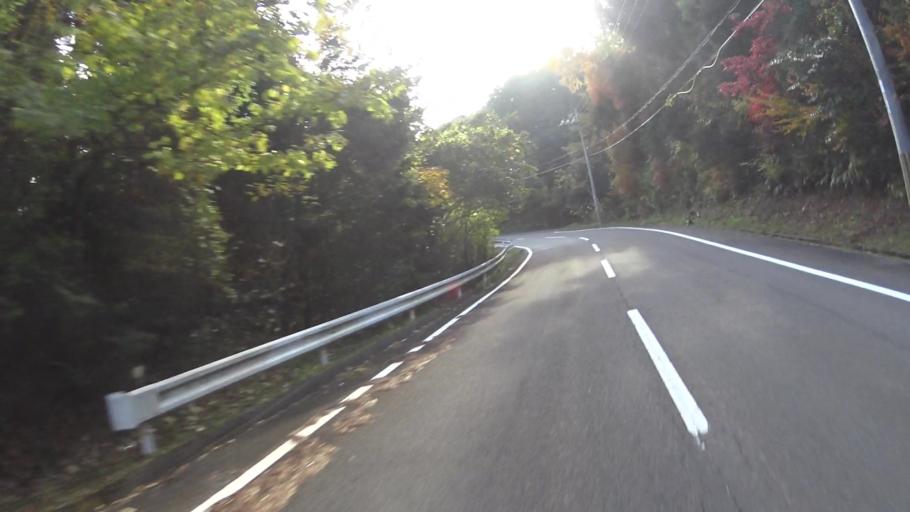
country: JP
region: Kyoto
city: Maizuru
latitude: 35.5475
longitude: 135.3960
